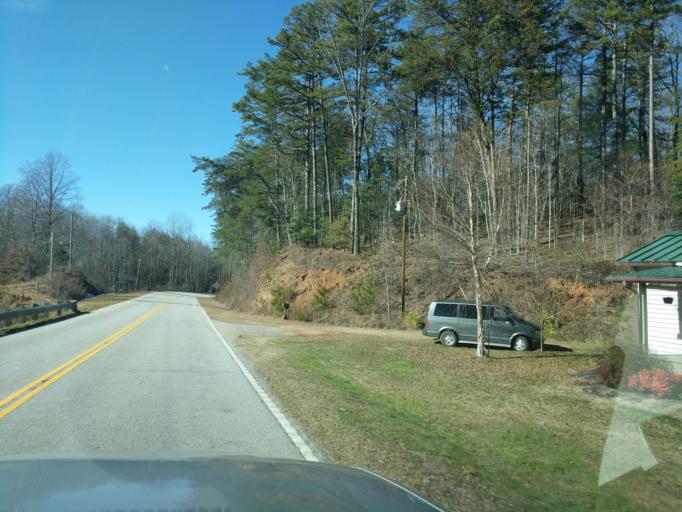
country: US
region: Georgia
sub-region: Rabun County
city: Clayton
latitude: 34.8059
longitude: -83.2762
